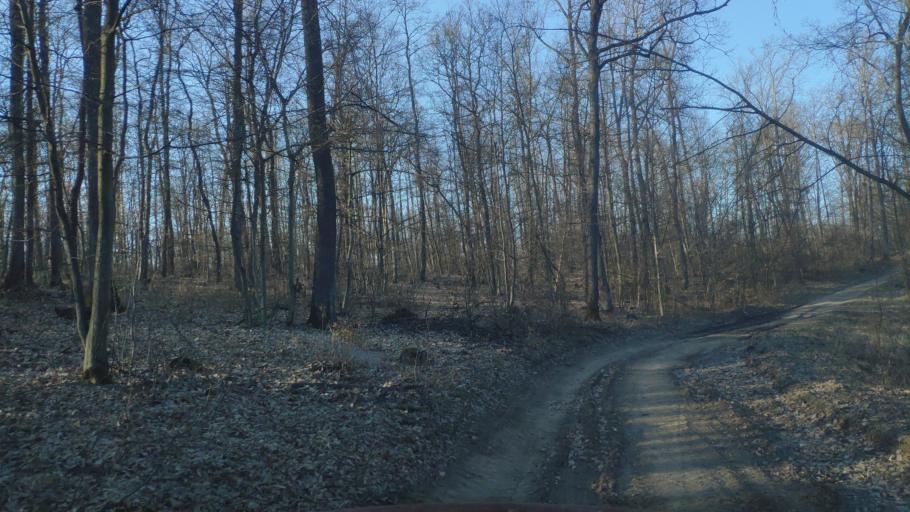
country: HU
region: Borsod-Abauj-Zemplen
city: Putnok
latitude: 48.5038
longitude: 20.3050
